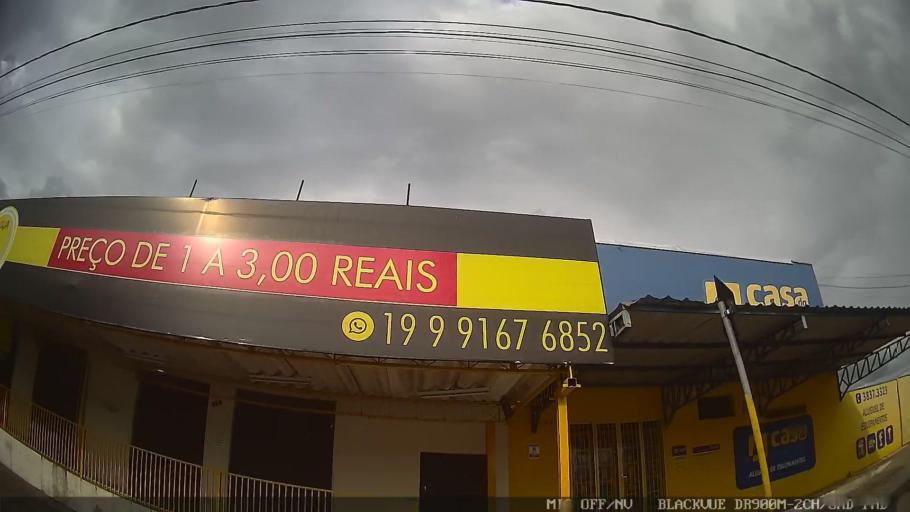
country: BR
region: Sao Paulo
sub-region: Jaguariuna
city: Jaguariuna
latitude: -22.6900
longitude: -46.9878
